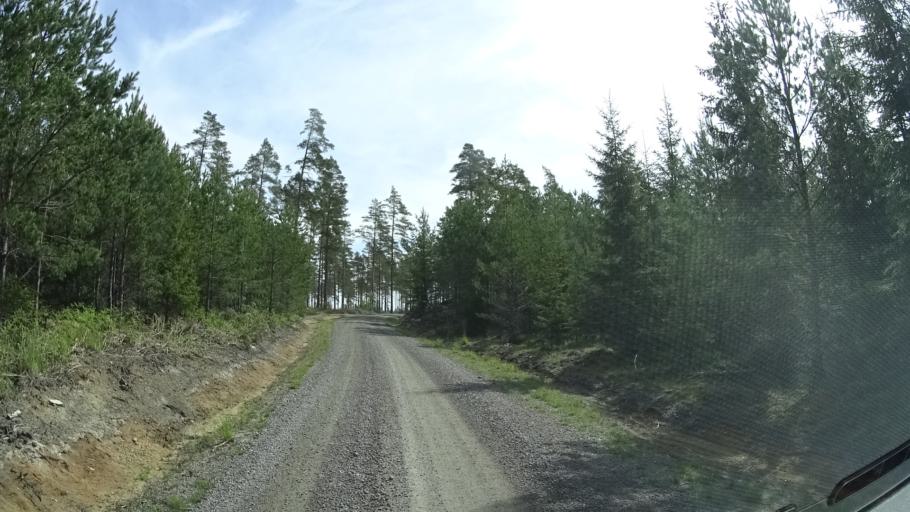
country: SE
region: OEstergoetland
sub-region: Finspangs Kommun
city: Finspang
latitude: 58.7811
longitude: 15.8774
